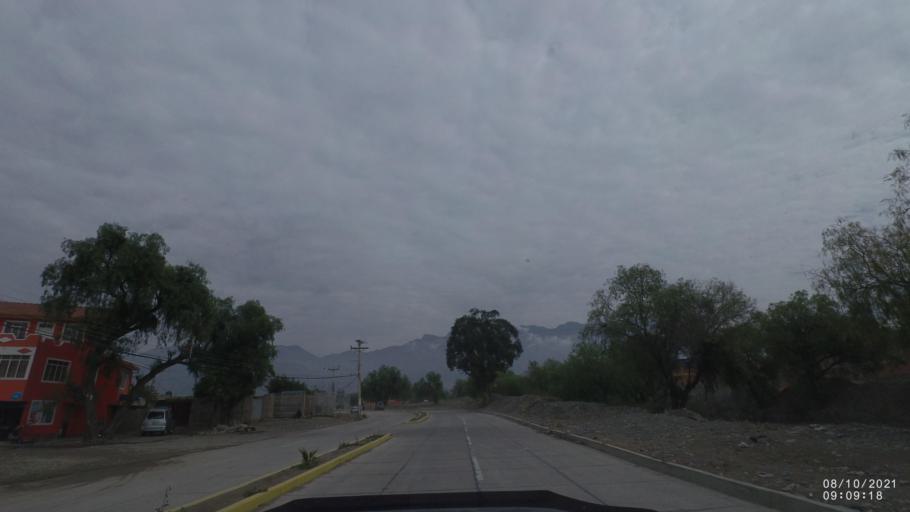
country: BO
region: Cochabamba
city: Sipe Sipe
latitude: -17.3968
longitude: -66.3268
